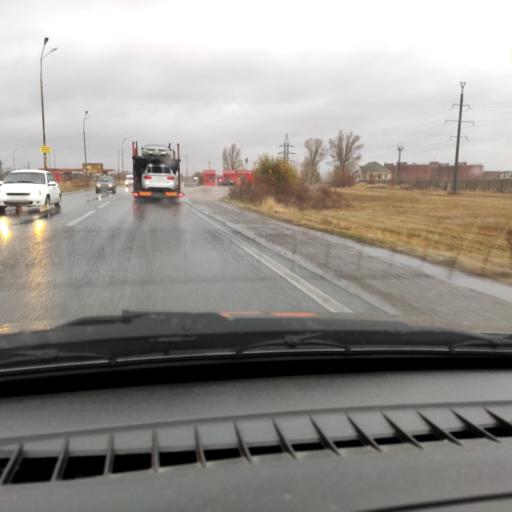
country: RU
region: Samara
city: Tol'yatti
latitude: 53.5704
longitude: 49.3445
